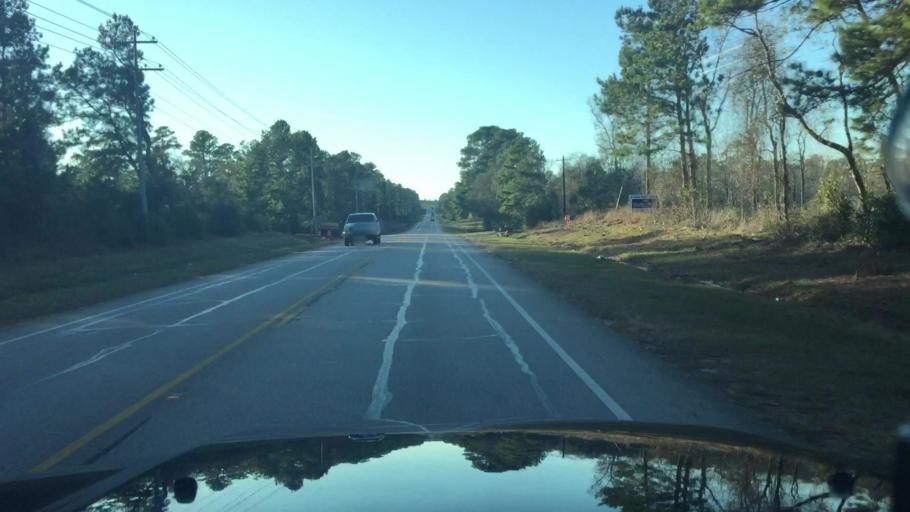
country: US
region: Texas
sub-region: Montgomery County
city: Panorama Village
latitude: 30.3183
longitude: -95.5581
